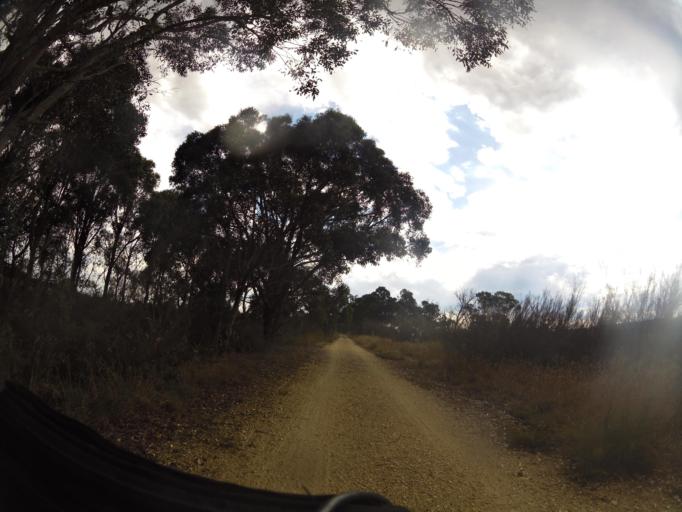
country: AU
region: Victoria
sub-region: Wellington
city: Heyfield
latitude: -38.0373
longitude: 146.6518
